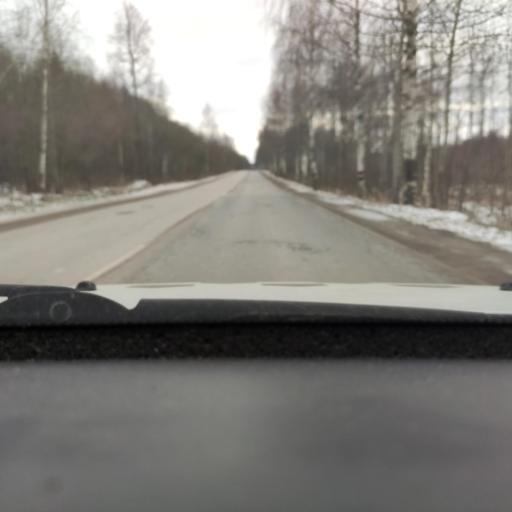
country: RU
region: Perm
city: Perm
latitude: 58.1020
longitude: 56.4125
